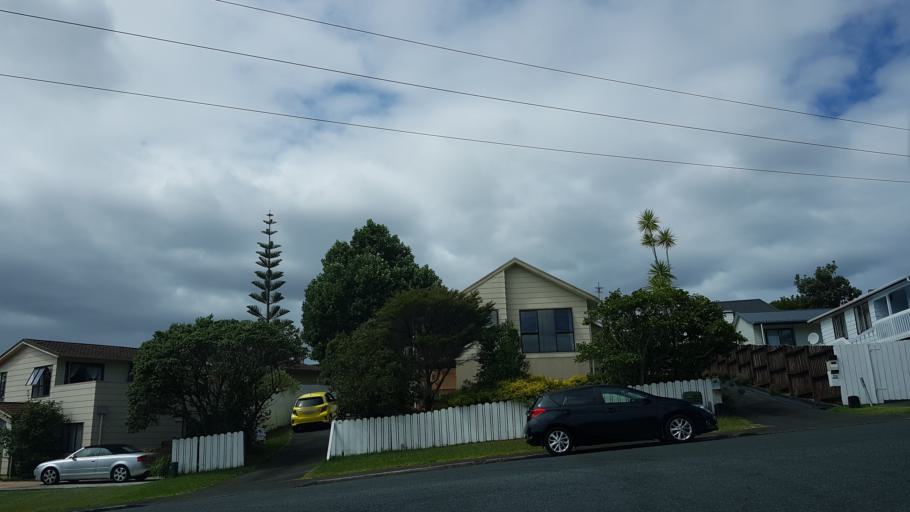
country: NZ
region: Auckland
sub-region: Auckland
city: North Shore
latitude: -36.7764
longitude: 174.7019
